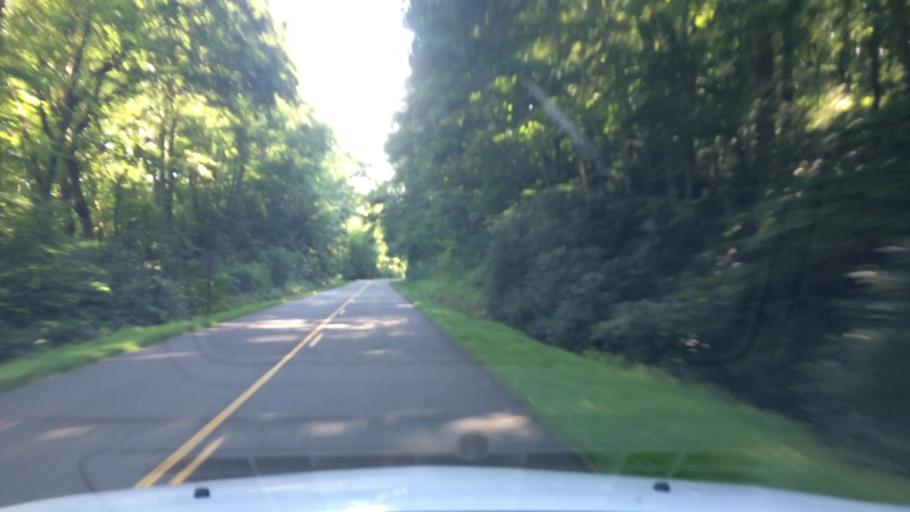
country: US
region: North Carolina
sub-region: Watauga County
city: Foscoe
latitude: 36.1359
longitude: -81.7401
